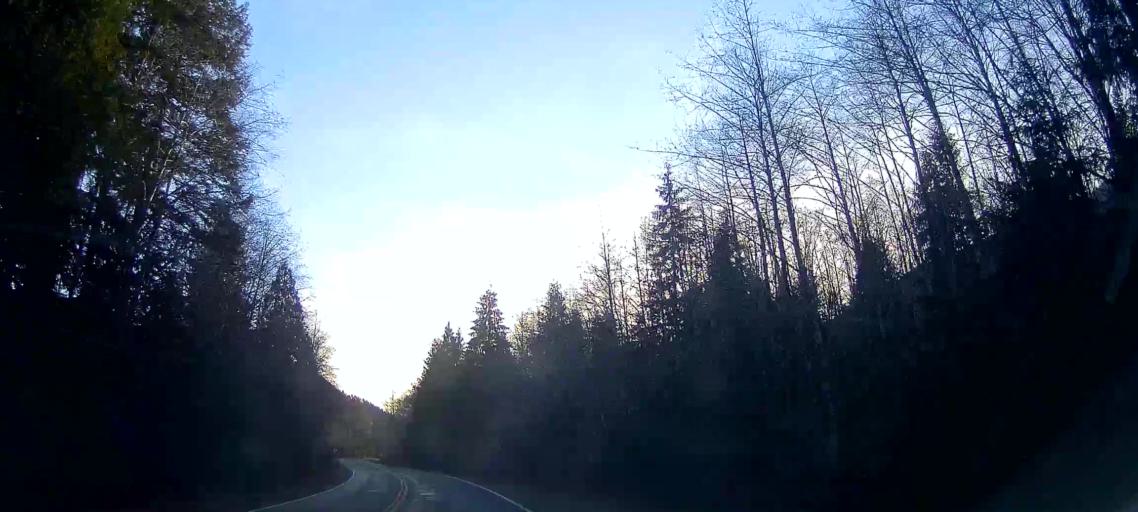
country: US
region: Washington
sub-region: Snohomish County
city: Darrington
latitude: 48.5974
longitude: -121.7696
